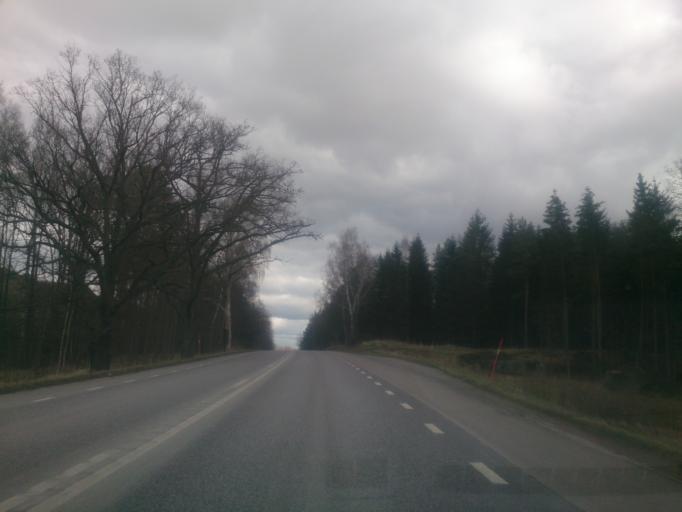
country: SE
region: OEstergoetland
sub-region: Norrkopings Kommun
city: Kimstad
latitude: 58.5607
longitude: 16.0744
